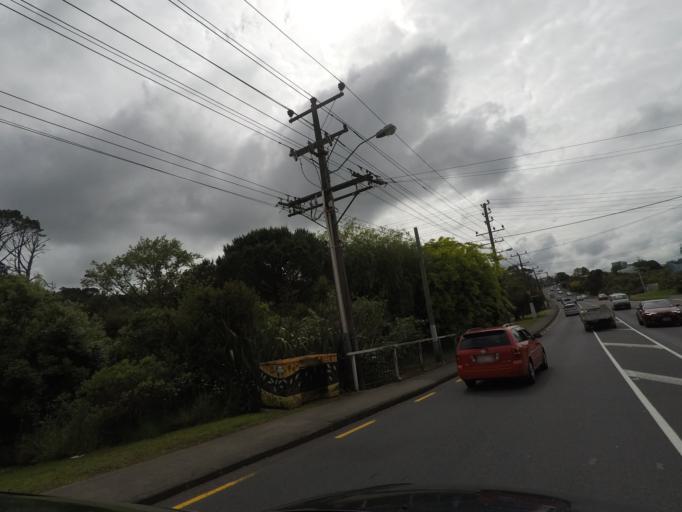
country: NZ
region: Auckland
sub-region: Auckland
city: Waitakere
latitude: -36.9084
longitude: 174.6420
